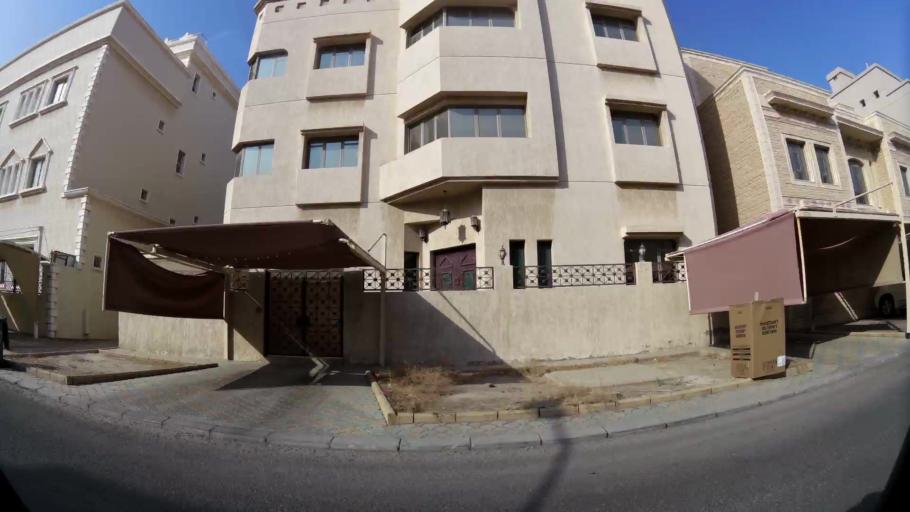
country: KW
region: Al Asimah
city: Ar Rabiyah
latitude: 29.2989
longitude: 47.8080
